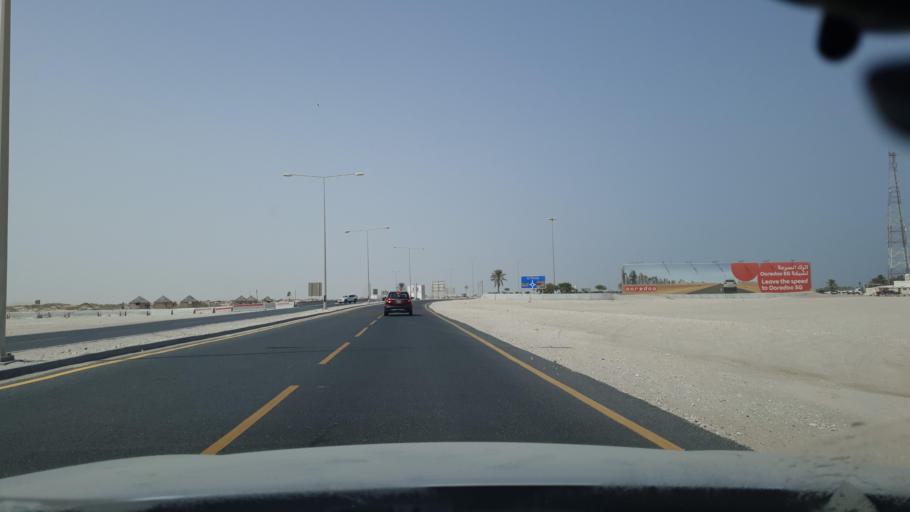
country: QA
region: Al Wakrah
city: Umm Sa'id
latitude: 24.8609
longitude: 51.5115
